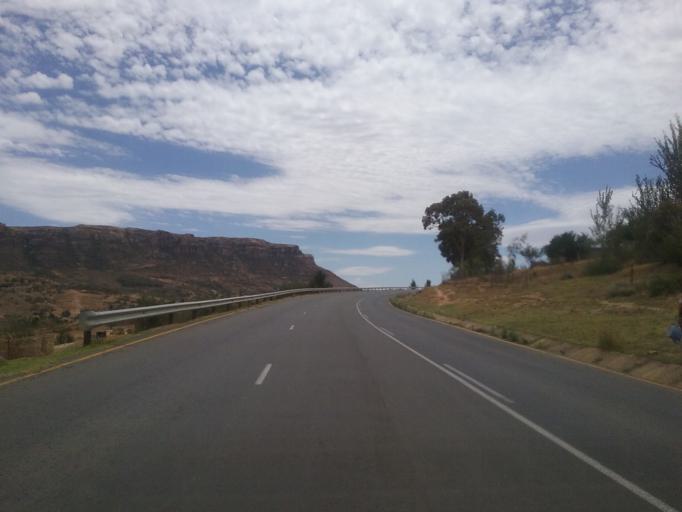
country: LS
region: Maseru
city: Maseru
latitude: -29.5126
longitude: 27.5235
